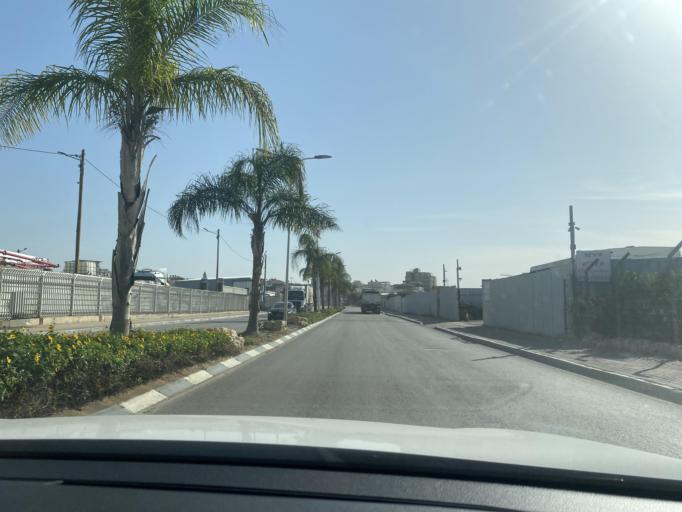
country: IL
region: Central District
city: Jaljulya
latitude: 32.1343
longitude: 34.9635
